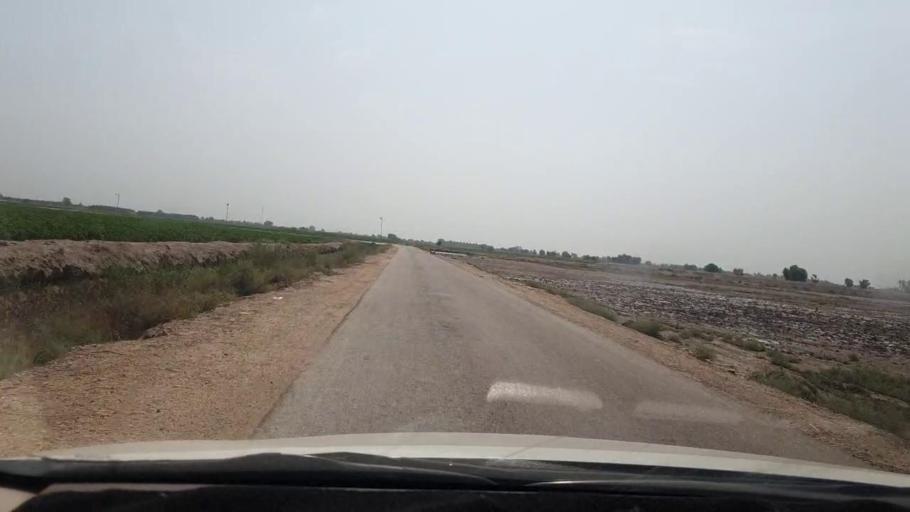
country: PK
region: Sindh
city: Rohri
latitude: 27.5382
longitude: 69.0089
